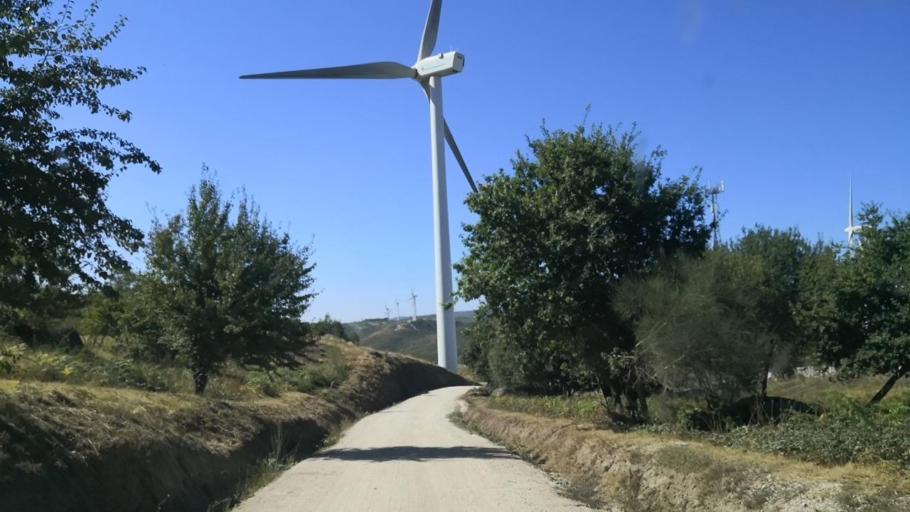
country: PT
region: Braga
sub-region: Cabeceiras de Basto
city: Refojos de Basto
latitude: 41.4917
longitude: -8.0710
